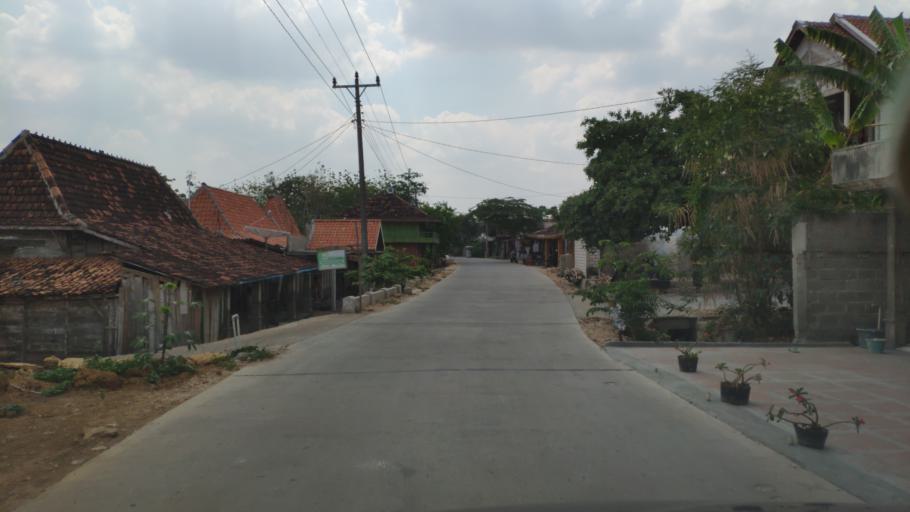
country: ID
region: Central Java
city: Ngapus
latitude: -6.9568
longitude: 111.1796
